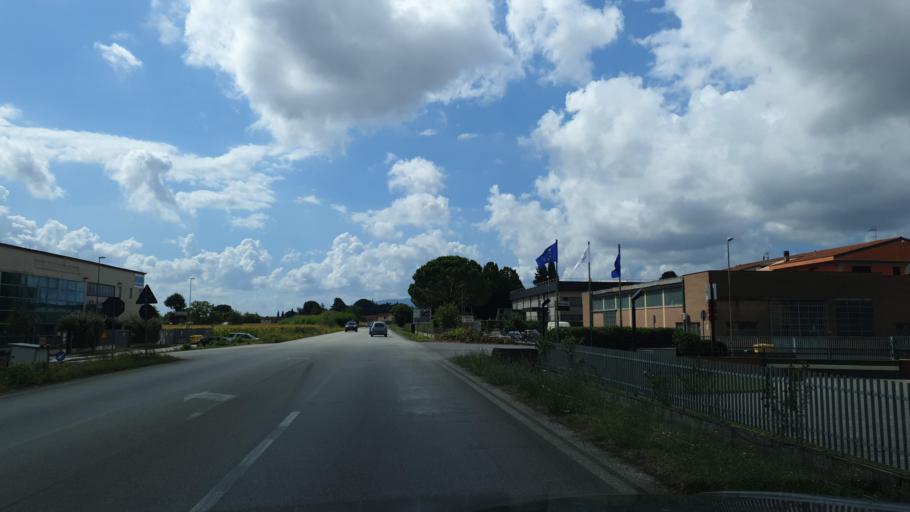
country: IT
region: Tuscany
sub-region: Provincia di Pistoia
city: Chiesina Uzzanese
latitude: 43.8457
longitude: 10.7287
